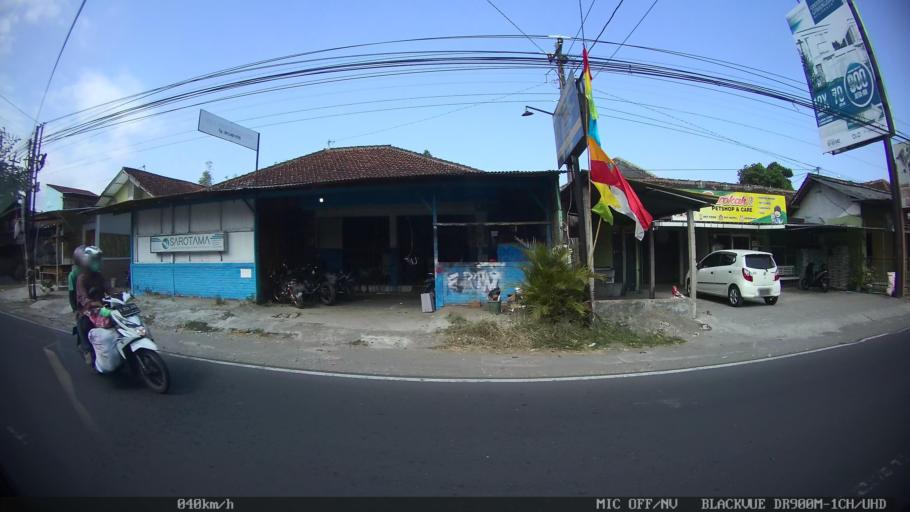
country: ID
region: Daerah Istimewa Yogyakarta
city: Sewon
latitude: -7.8622
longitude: 110.3894
